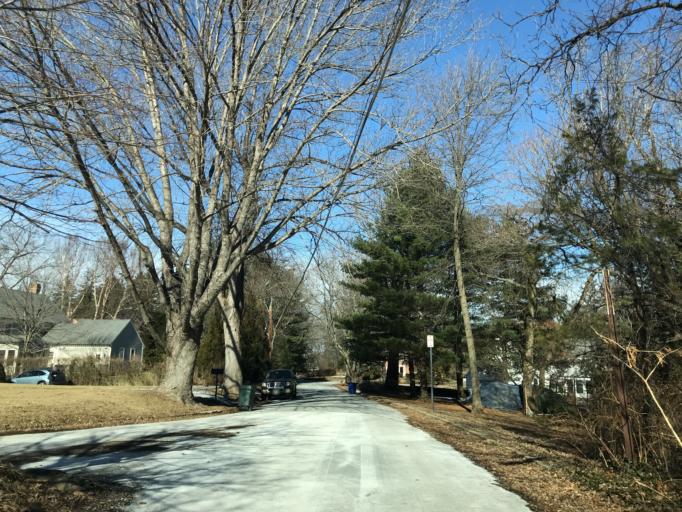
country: US
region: Maryland
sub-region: Baltimore County
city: Towson
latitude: 39.3724
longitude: -76.6373
